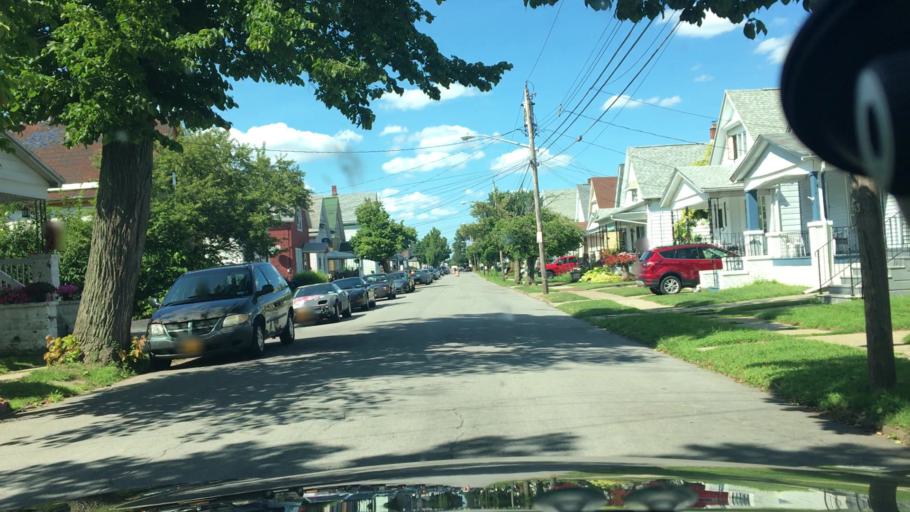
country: US
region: New York
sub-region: Erie County
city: West Seneca
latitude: 42.8689
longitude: -78.8059
